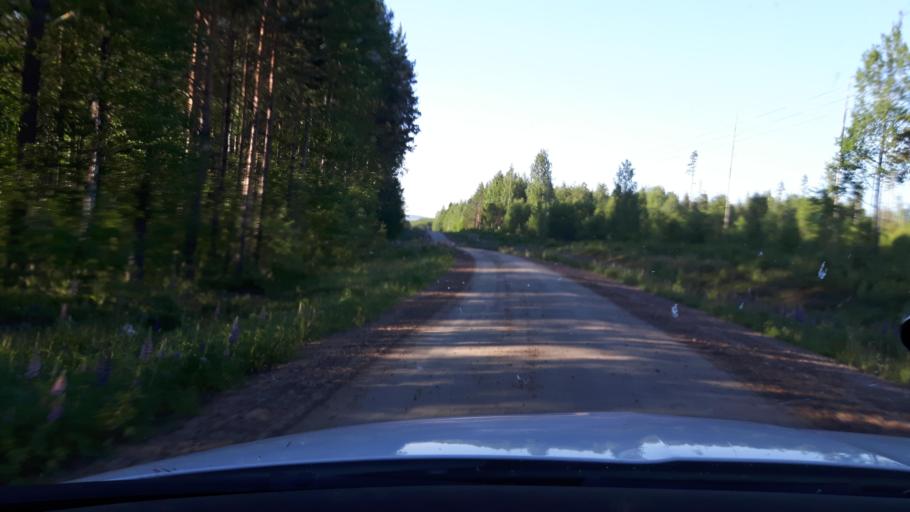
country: SE
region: Vaesternorrland
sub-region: Ange Kommun
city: Ange
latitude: 62.1628
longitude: 15.6589
